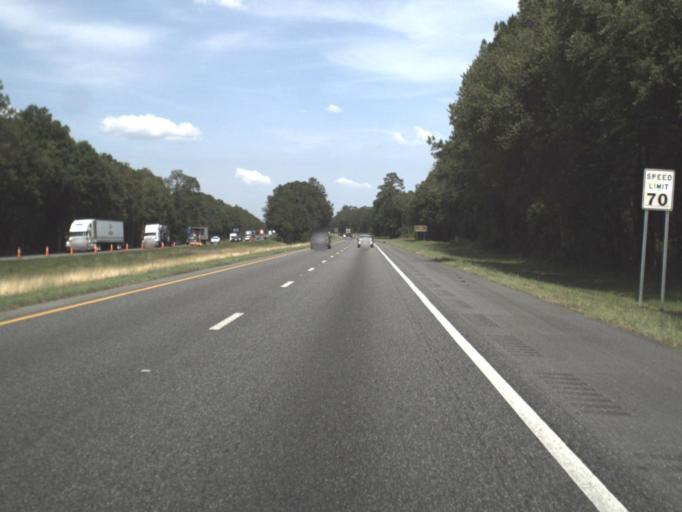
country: US
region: Florida
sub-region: Columbia County
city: Five Points
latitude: 30.2408
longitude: -82.6119
